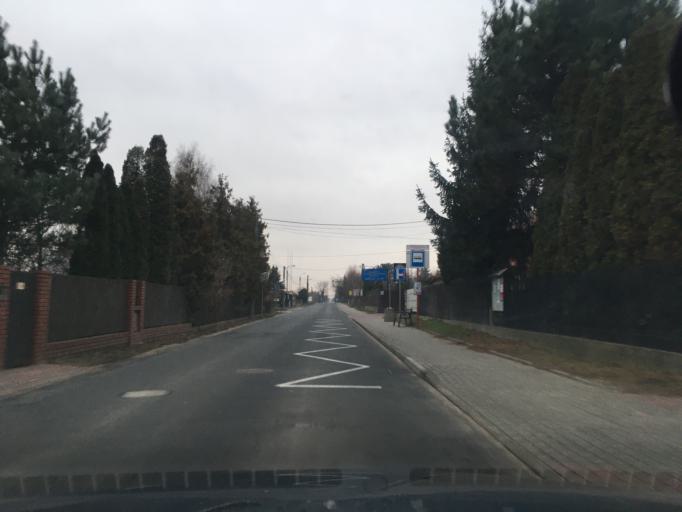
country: PL
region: Masovian Voivodeship
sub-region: Powiat piaseczynski
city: Mysiadlo
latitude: 52.1277
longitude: 20.9797
